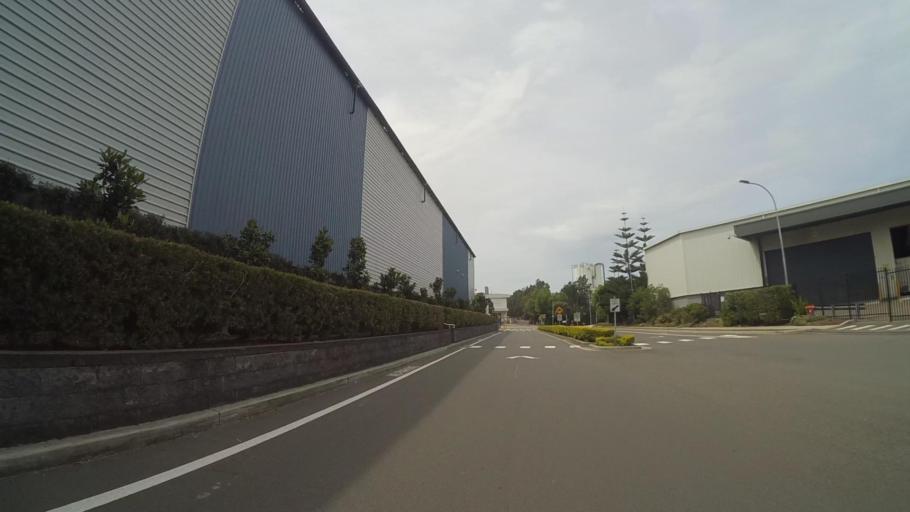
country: AU
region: New South Wales
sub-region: Botany Bay
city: Mascot
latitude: -33.9235
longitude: 151.1774
